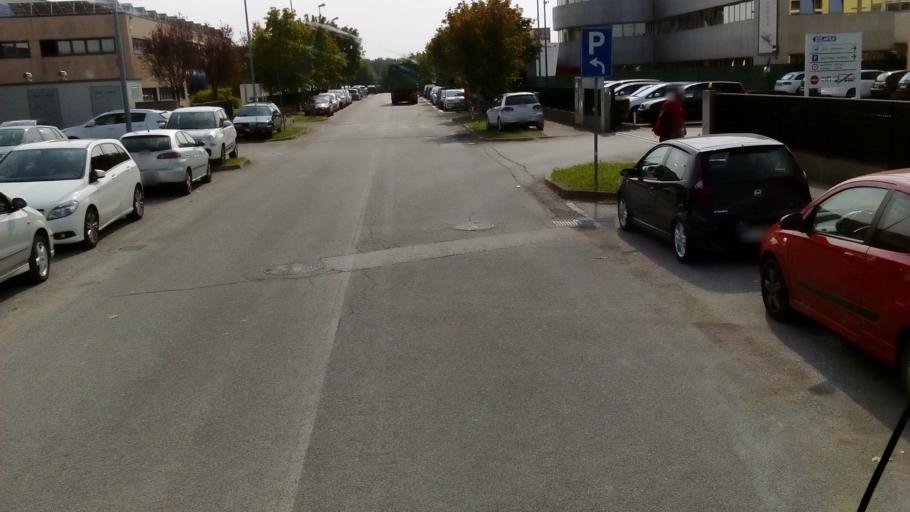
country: IT
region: Veneto
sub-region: Provincia di Padova
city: Tribano
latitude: 45.2103
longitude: 11.8456
